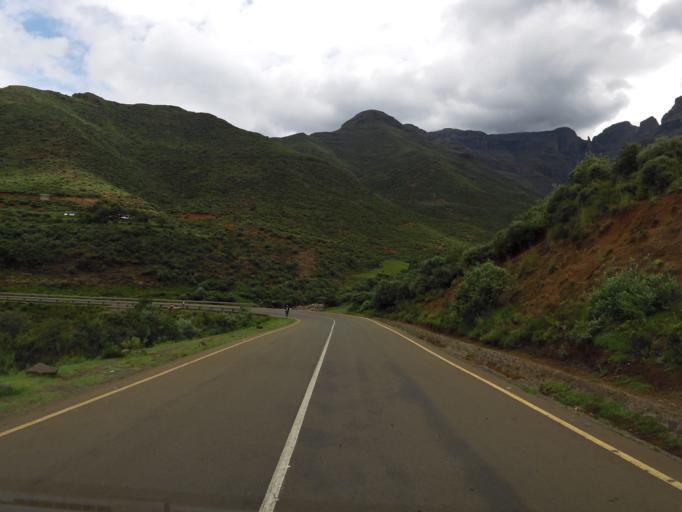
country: LS
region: Butha-Buthe
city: Butha-Buthe
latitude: -29.0470
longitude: 28.3115
